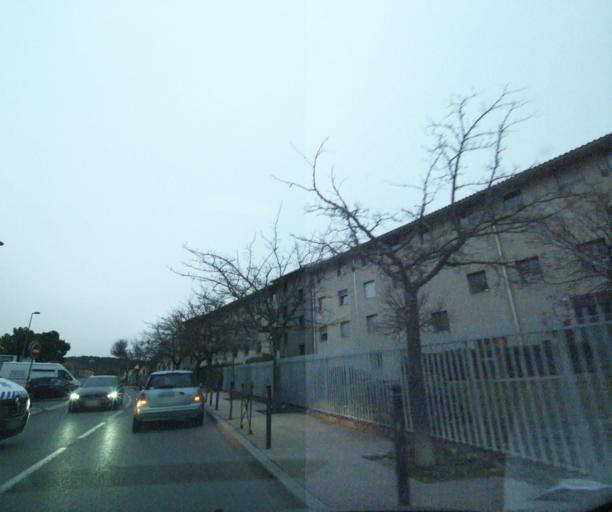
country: FR
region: Provence-Alpes-Cote d'Azur
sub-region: Departement des Bouches-du-Rhone
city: Aix-en-Provence
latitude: 43.5303
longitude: 5.4576
